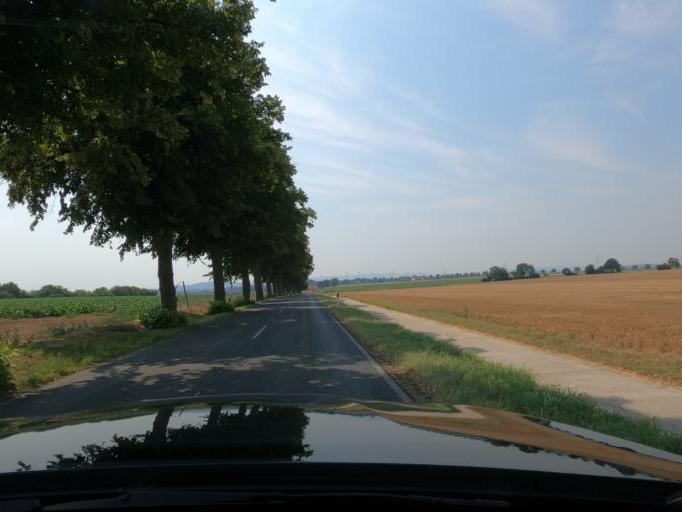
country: DE
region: Lower Saxony
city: Sarstedt
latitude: 52.2263
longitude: 9.8087
